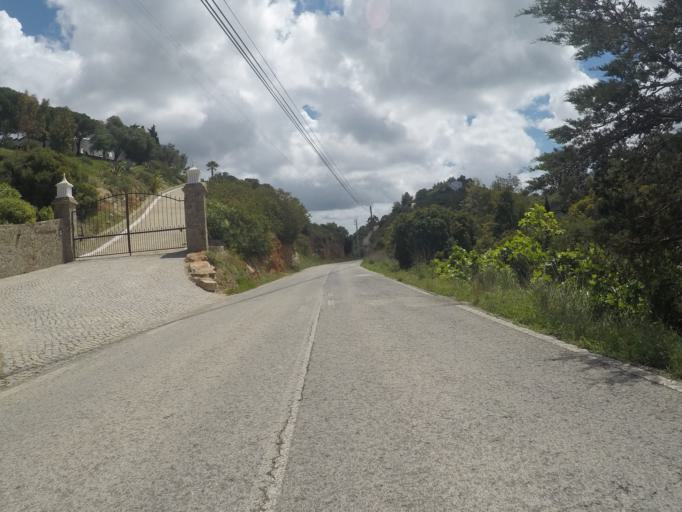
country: PT
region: Faro
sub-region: Vila do Bispo
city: Vila do Bispo
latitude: 37.0732
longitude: -8.8294
